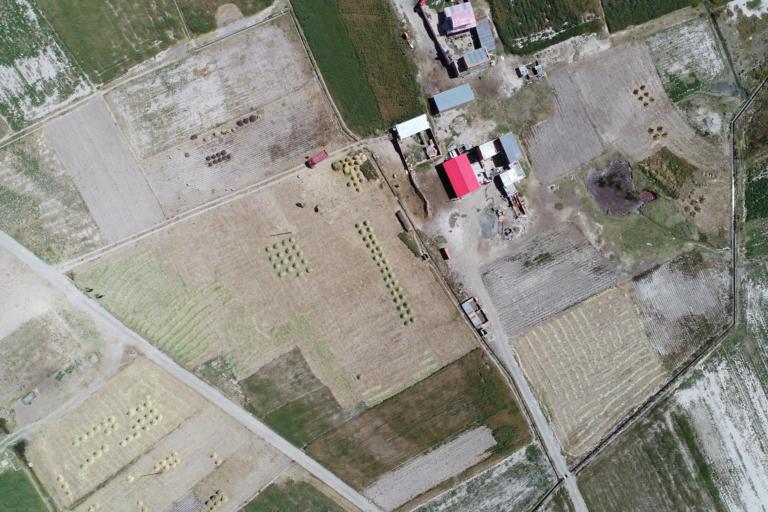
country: BO
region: La Paz
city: Achacachi
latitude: -16.0175
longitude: -68.7186
